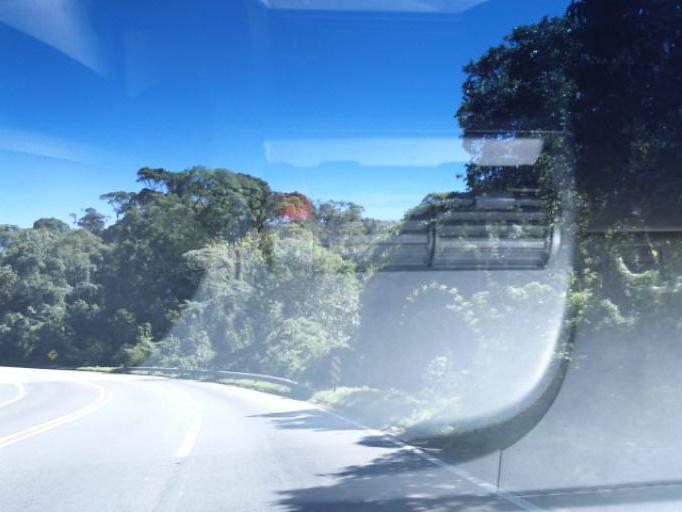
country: BR
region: Sao Paulo
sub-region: Campos Do Jordao
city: Campos do Jordao
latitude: -22.8208
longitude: -45.6232
